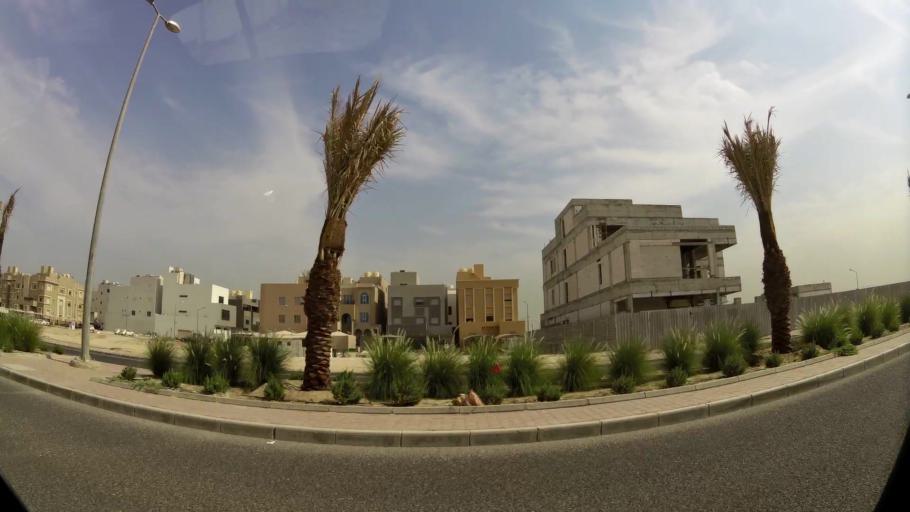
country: KW
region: Al Farwaniyah
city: Janub as Surrah
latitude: 29.2933
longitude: 47.9974
